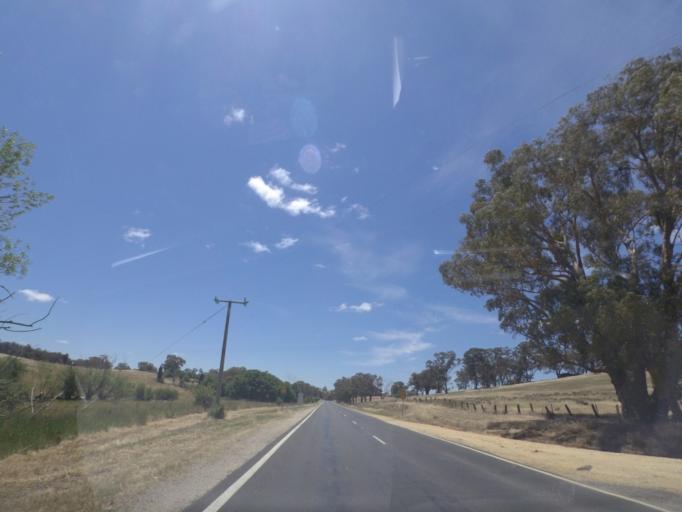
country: AU
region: Victoria
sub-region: Mount Alexander
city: Castlemaine
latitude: -37.1570
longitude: 144.1598
